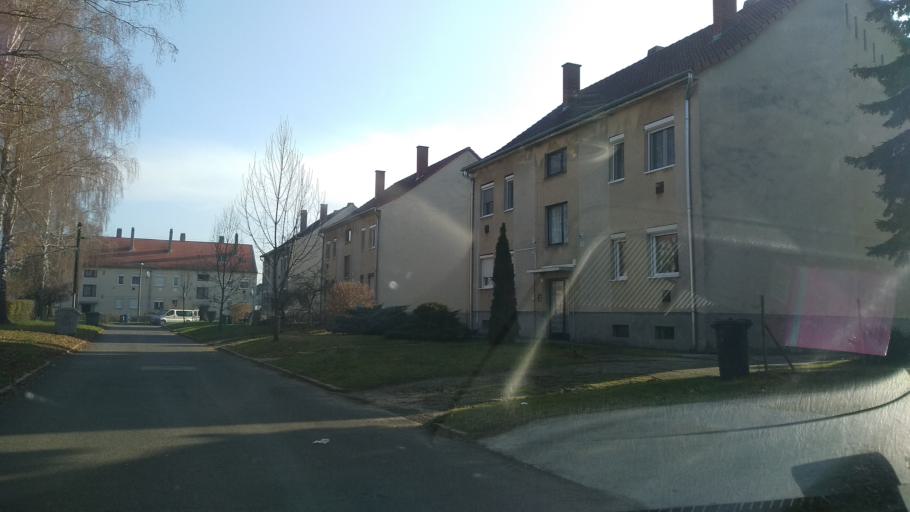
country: HU
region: Somogy
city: Barcs
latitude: 45.9615
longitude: 17.4564
